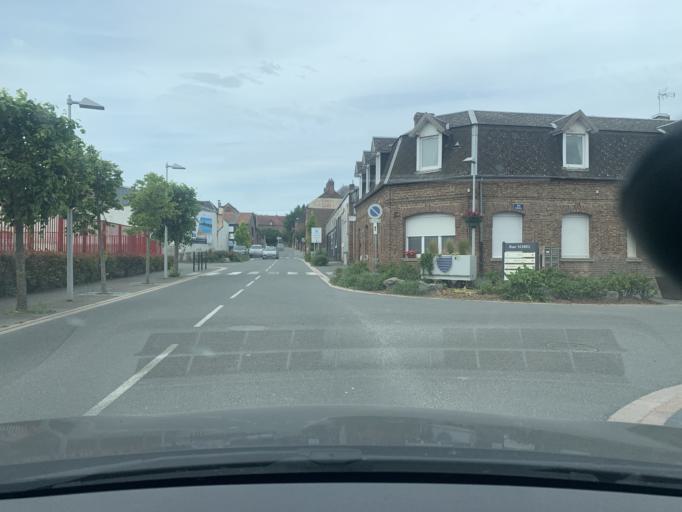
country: FR
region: Nord-Pas-de-Calais
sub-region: Departement du Nord
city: Marcoing
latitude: 50.1381
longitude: 3.1837
